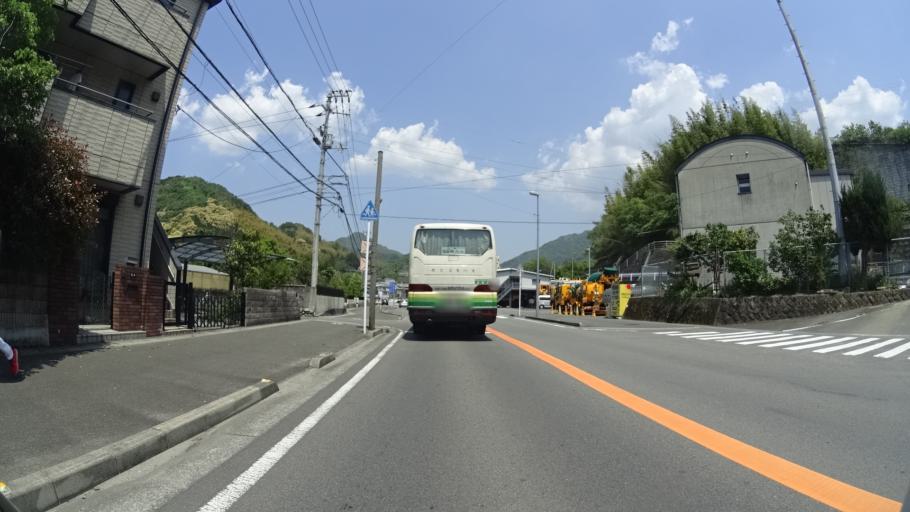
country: JP
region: Ehime
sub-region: Shikoku-chuo Shi
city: Matsuyama
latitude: 33.8616
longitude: 132.8163
